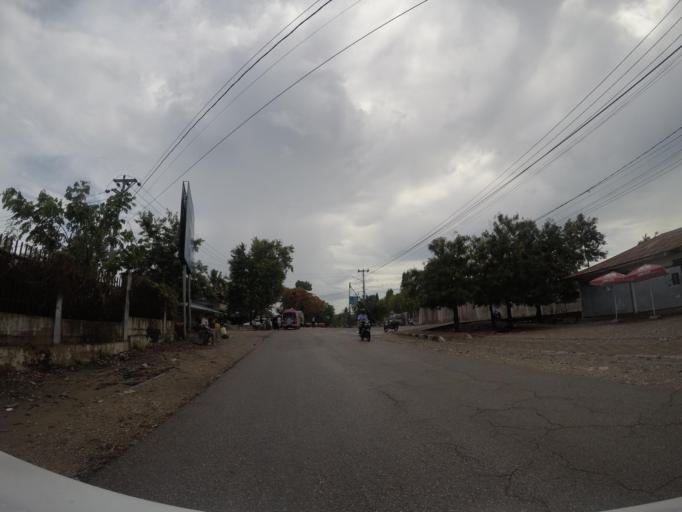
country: TL
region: Baucau
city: Baucau
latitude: -8.4759
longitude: 126.4584
